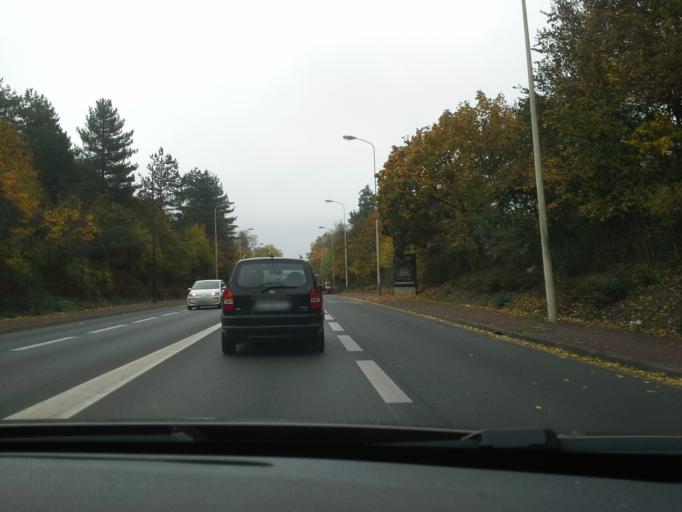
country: FR
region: Centre
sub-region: Departement d'Indre-et-Loire
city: Tours
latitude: 47.4077
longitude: 0.7032
